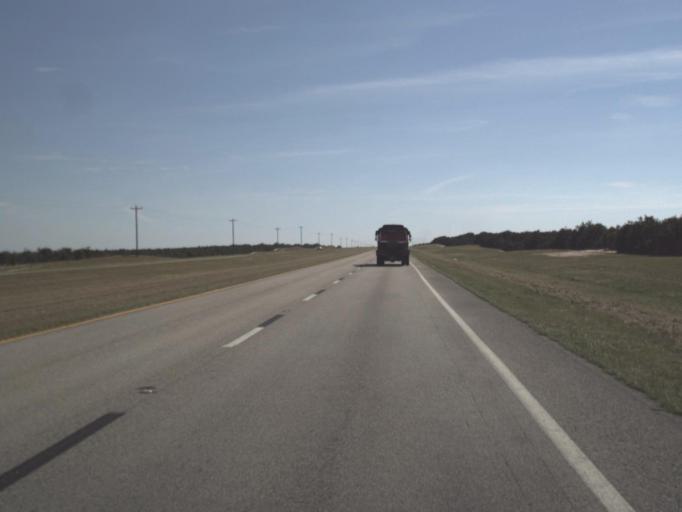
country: US
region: Florida
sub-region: Highlands County
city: Placid Lakes
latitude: 27.1637
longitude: -81.3289
